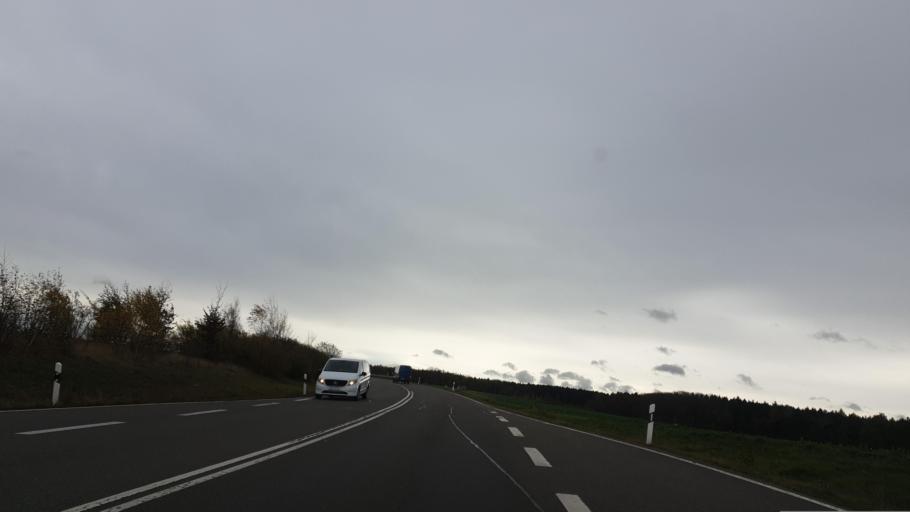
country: DE
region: Saxony
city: Neumark
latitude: 50.6429
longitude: 12.3393
